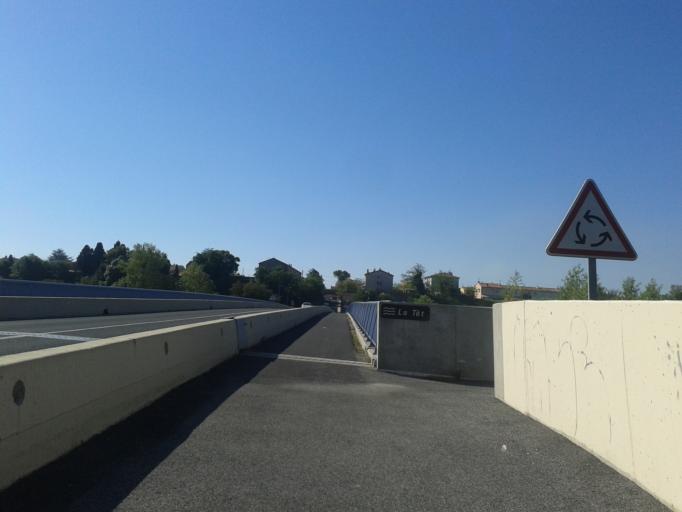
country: FR
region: Languedoc-Roussillon
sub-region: Departement des Pyrenees-Orientales
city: Le Soler
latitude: 42.6854
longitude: 2.7904
